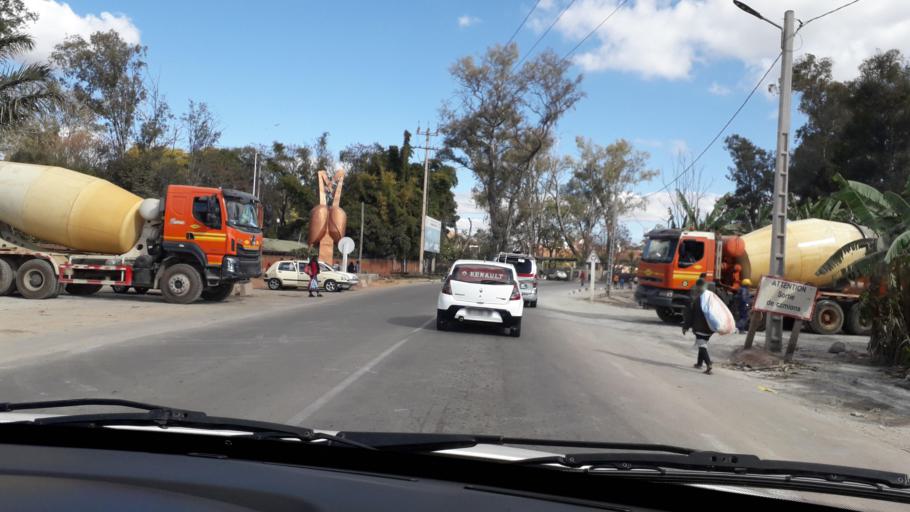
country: MG
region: Analamanga
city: Antananarivo
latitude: -18.8677
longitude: 47.5160
